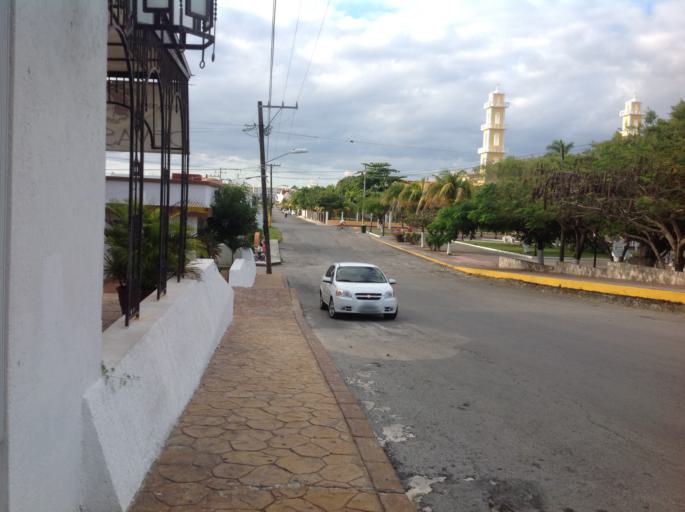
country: MX
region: Quintana Roo
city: San Miguel de Cozumel
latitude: 20.4989
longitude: -86.9541
